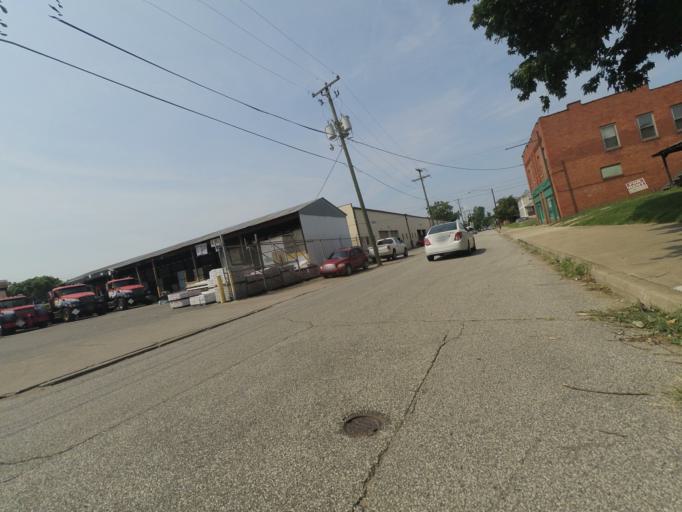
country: US
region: West Virginia
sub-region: Cabell County
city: Huntington
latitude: 38.4195
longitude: -82.4270
